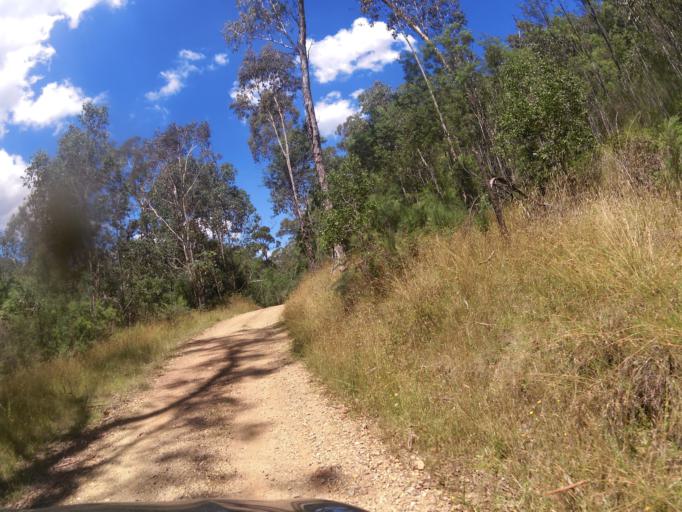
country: AU
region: Victoria
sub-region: Alpine
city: Mount Beauty
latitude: -36.7712
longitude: 147.0490
